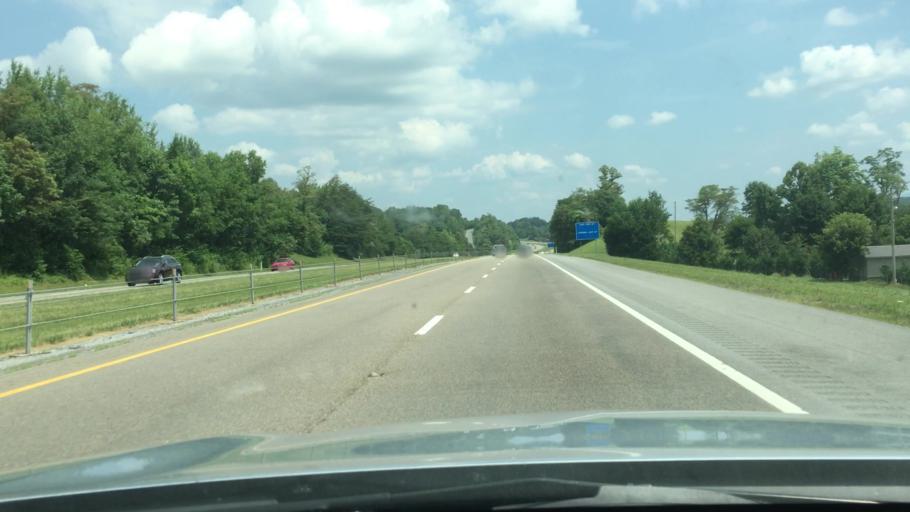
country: US
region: Tennessee
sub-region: Carter County
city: Pine Crest
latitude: 36.2466
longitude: -82.3256
